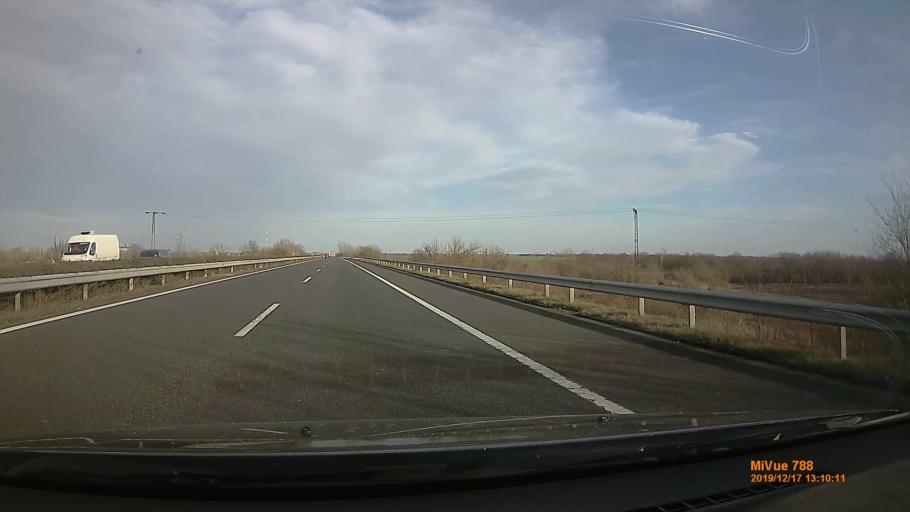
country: HU
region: Somogy
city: Siofok
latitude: 46.9024
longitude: 18.0770
